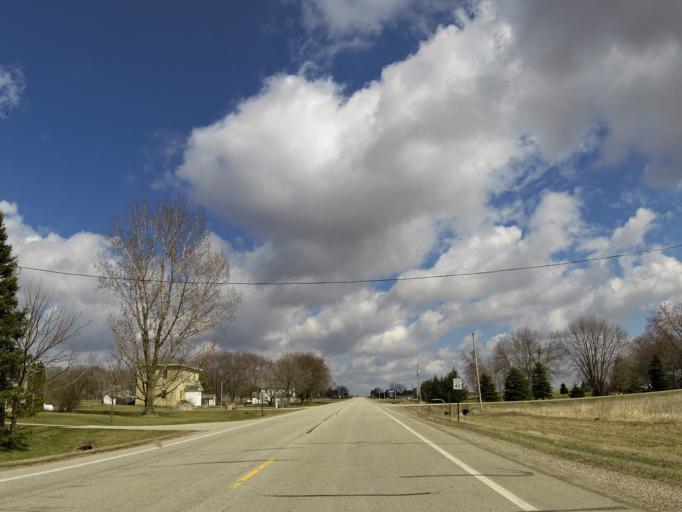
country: US
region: Minnesota
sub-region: Dodge County
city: Dodge Center
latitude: 44.0805
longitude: -92.8186
